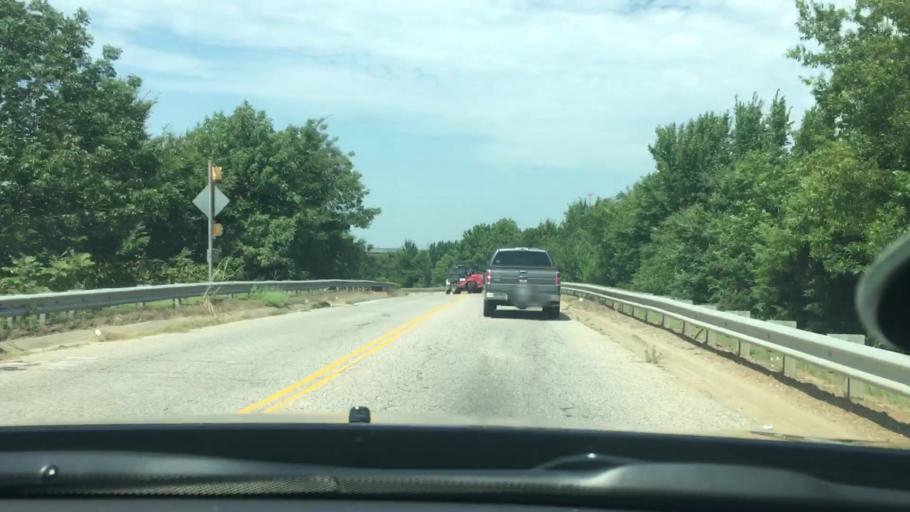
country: US
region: Oklahoma
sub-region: Pontotoc County
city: Ada
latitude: 34.7914
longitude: -96.6438
